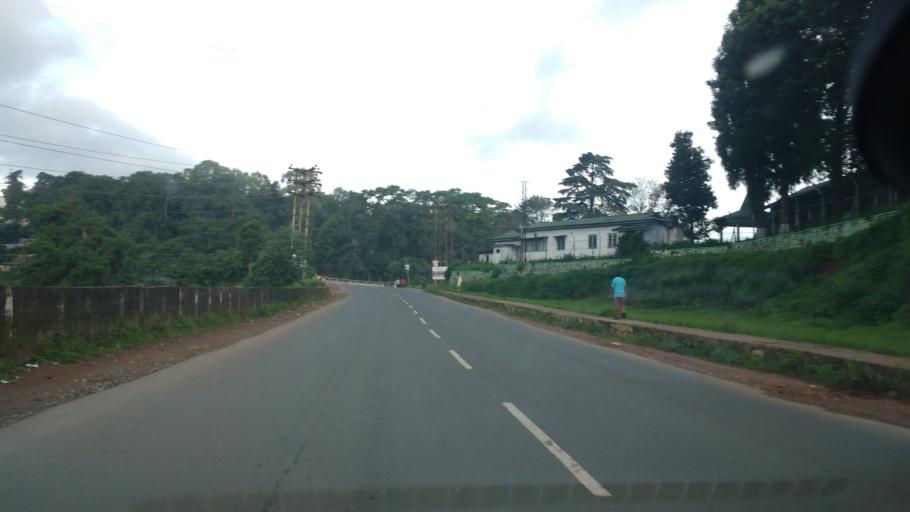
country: IN
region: Meghalaya
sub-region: East Khasi Hills
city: Shillong
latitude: 25.5717
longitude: 91.8701
